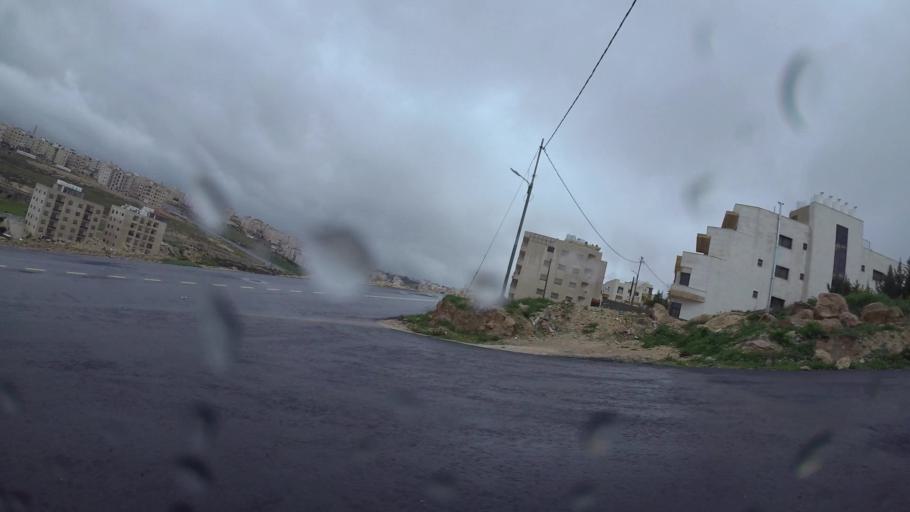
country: JO
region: Amman
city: Al Jubayhah
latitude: 32.0415
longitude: 35.8885
